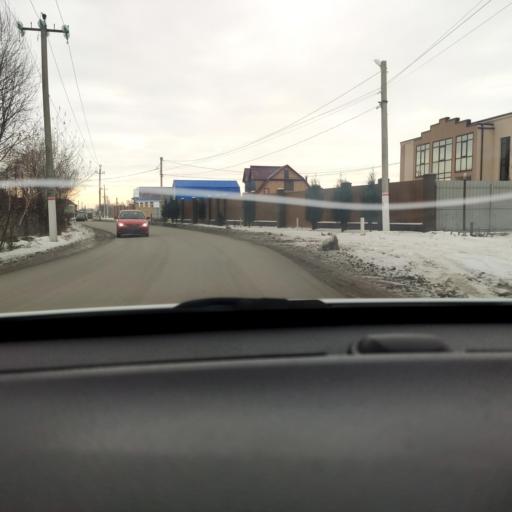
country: RU
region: Voronezj
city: Somovo
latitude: 51.6745
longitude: 39.3349
